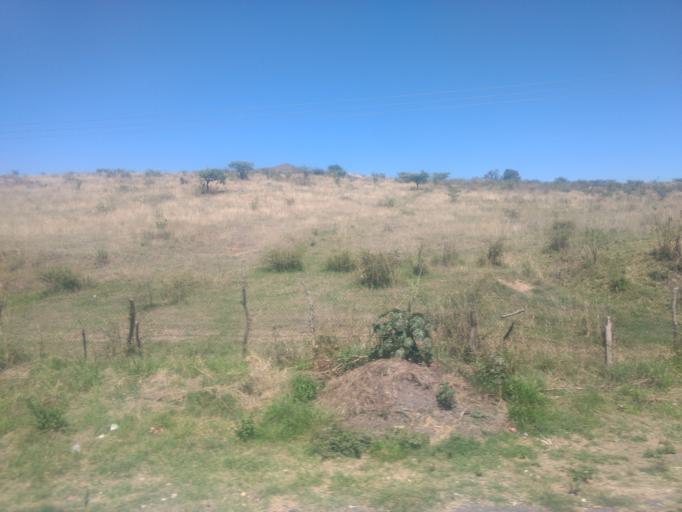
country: MX
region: Jalisco
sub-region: Tlajomulco de Zuniga
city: Santa Cruz de las Flores
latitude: 20.5015
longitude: -103.4883
